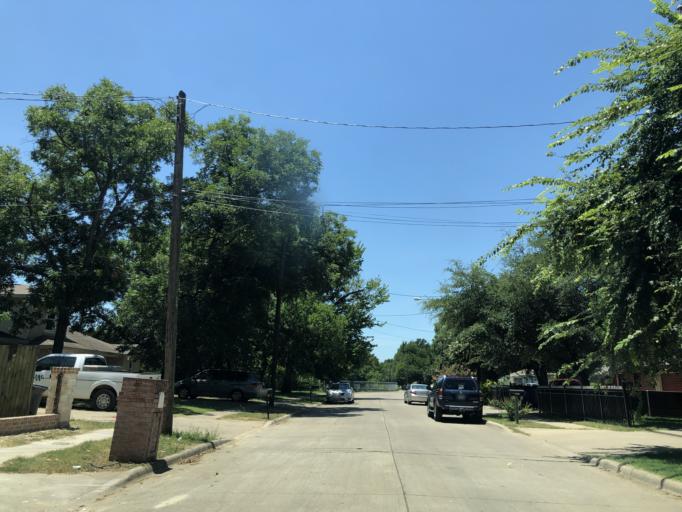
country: US
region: Texas
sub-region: Dallas County
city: Irving
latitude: 32.7949
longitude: -96.9020
